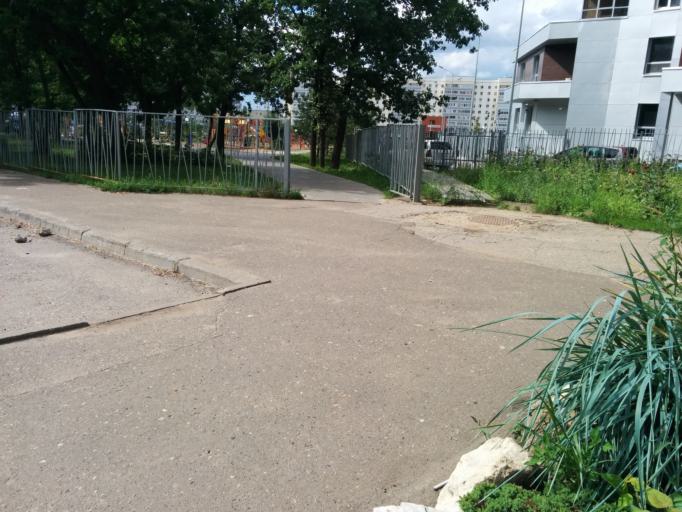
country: RU
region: Tatarstan
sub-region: Gorod Kazan'
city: Kazan
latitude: 55.7463
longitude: 49.2063
